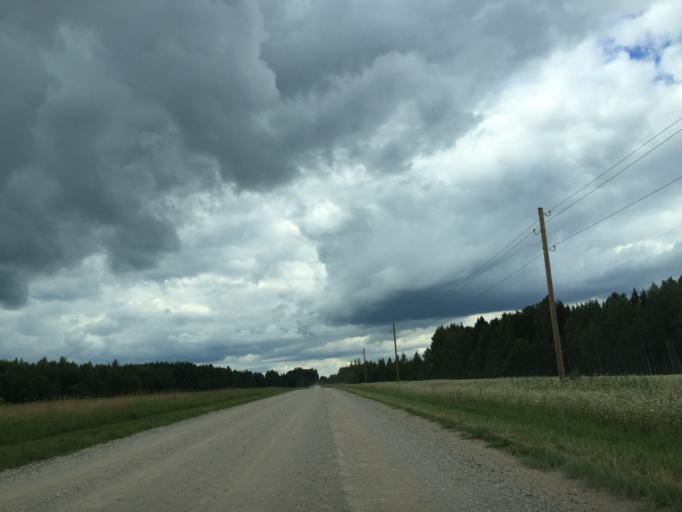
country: LV
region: Malpils
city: Malpils
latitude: 56.8657
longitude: 25.0125
